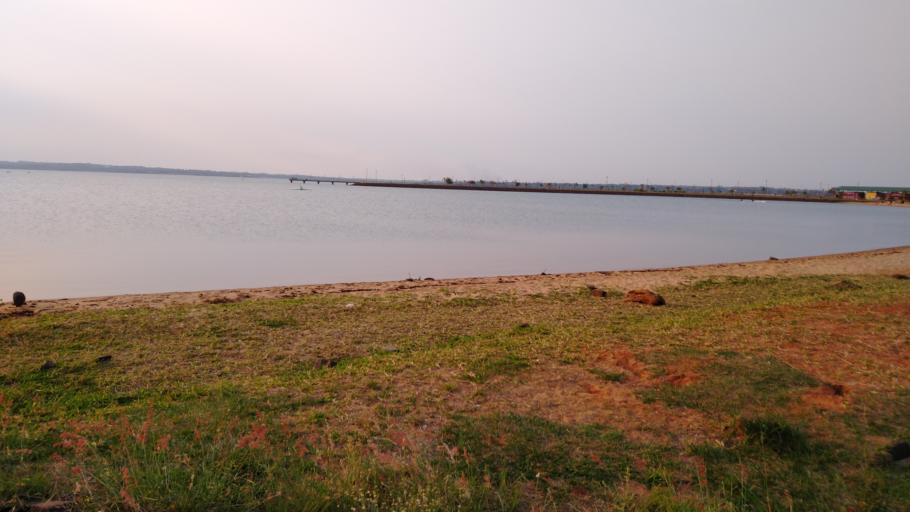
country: AR
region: Misiones
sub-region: Departamento de Capital
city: Posadas
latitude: -27.3562
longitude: -55.9050
